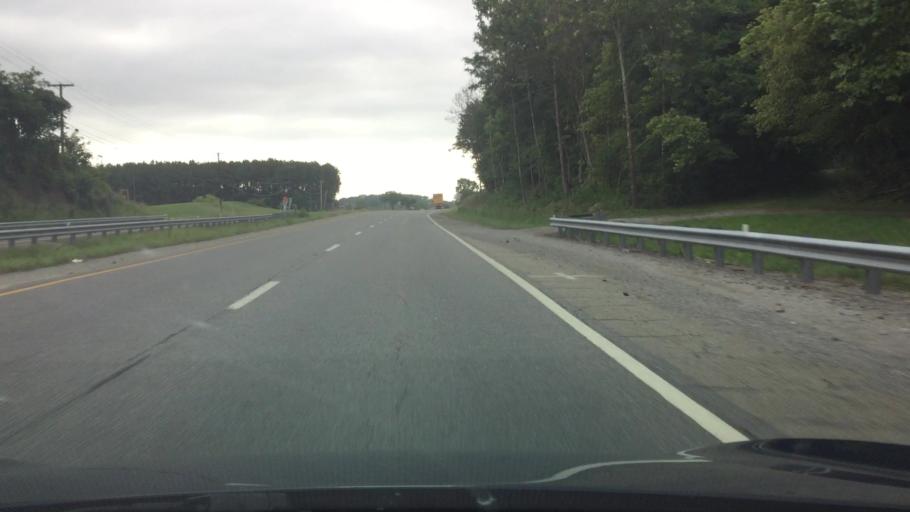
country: US
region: Virginia
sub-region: Montgomery County
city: Shawsville
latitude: 37.2278
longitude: -80.2079
